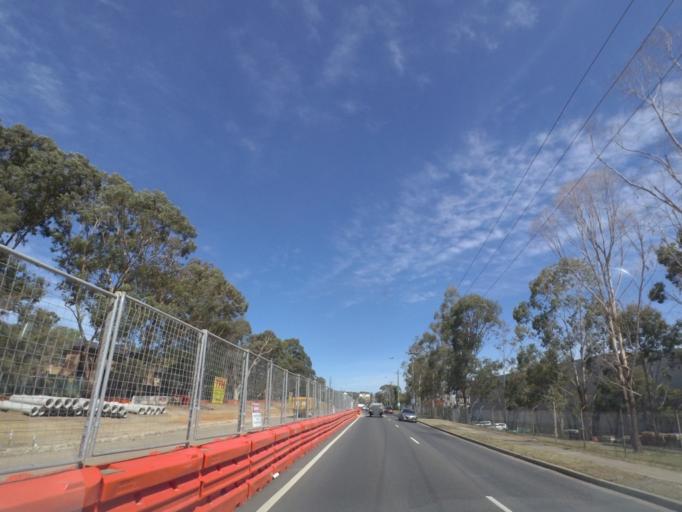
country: AU
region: New South Wales
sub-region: Campbelltown Municipality
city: Campbelltown
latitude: -34.0546
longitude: 150.8092
